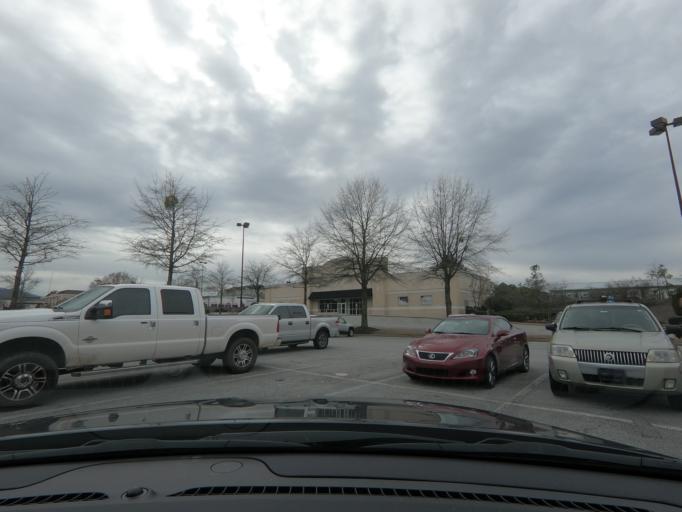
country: US
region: Georgia
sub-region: Cobb County
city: Kennesaw
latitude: 34.0130
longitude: -84.5731
